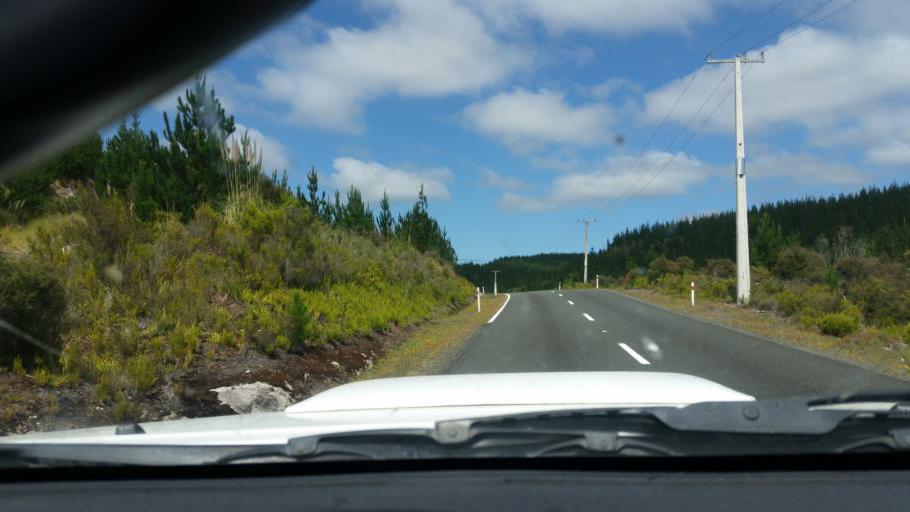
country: NZ
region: Northland
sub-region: Kaipara District
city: Dargaville
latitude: -35.8174
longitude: 173.7132
